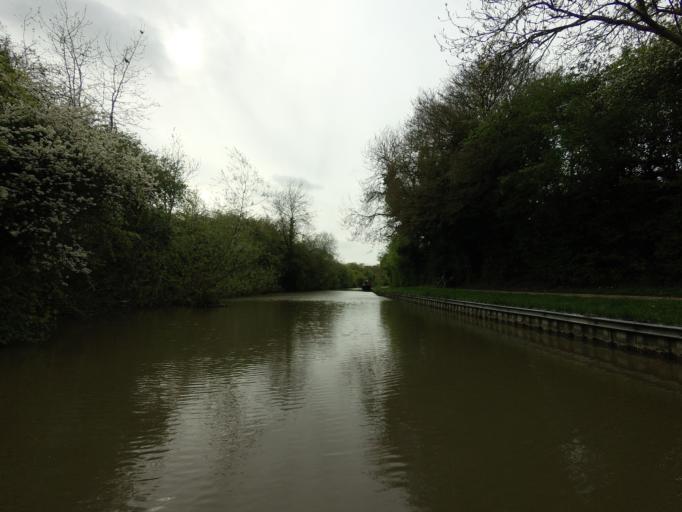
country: GB
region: England
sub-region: Milton Keynes
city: Bradwell
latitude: 52.0600
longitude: -0.7989
